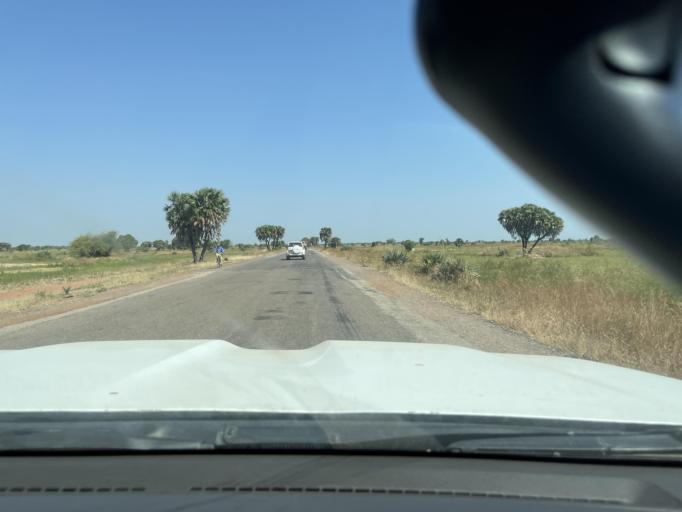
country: TD
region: Tandjile
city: Kelo
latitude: 9.5480
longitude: 15.8182
